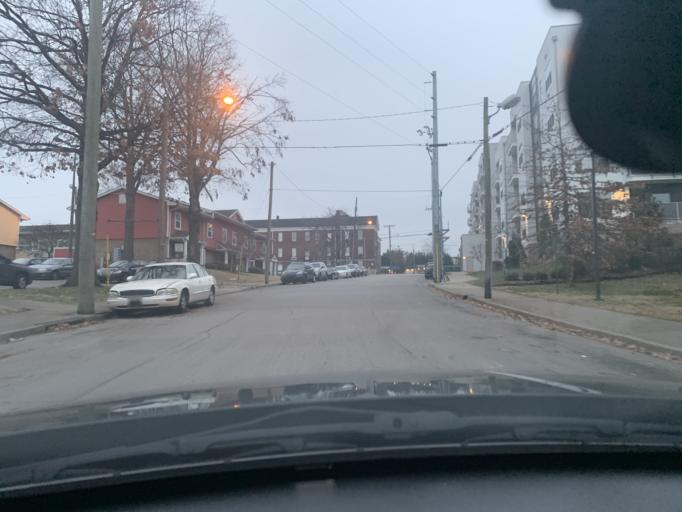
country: US
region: Tennessee
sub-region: Davidson County
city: Nashville
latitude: 36.1751
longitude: -86.7637
